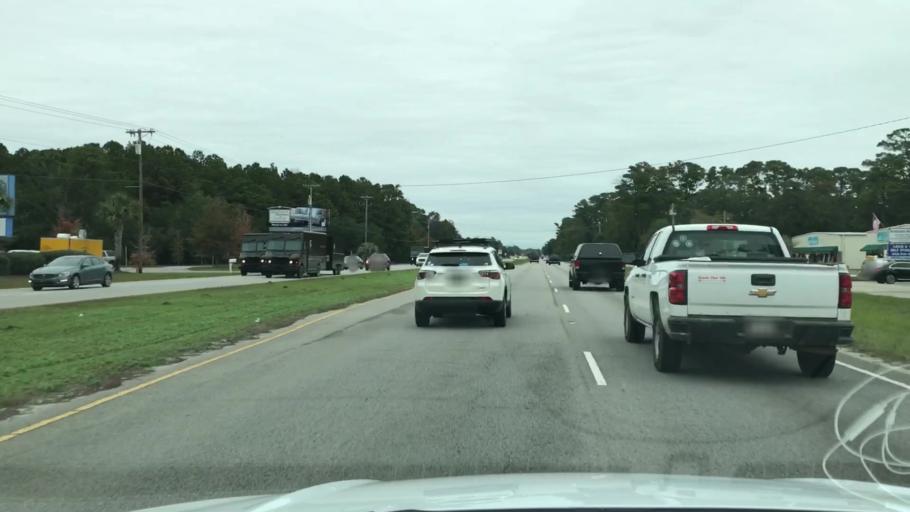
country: US
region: South Carolina
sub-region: Georgetown County
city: Murrells Inlet
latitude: 33.5410
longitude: -79.0541
